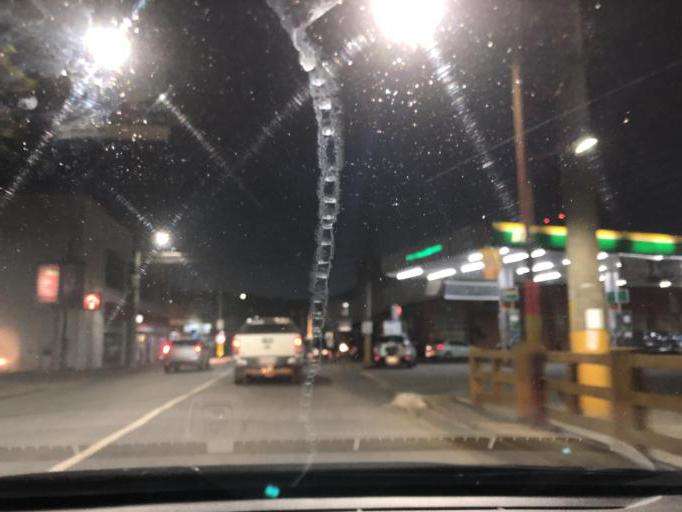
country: BR
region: Santa Catarina
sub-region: Jaragua Do Sul
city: Jaragua do Sul
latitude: -26.4803
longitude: -49.0810
